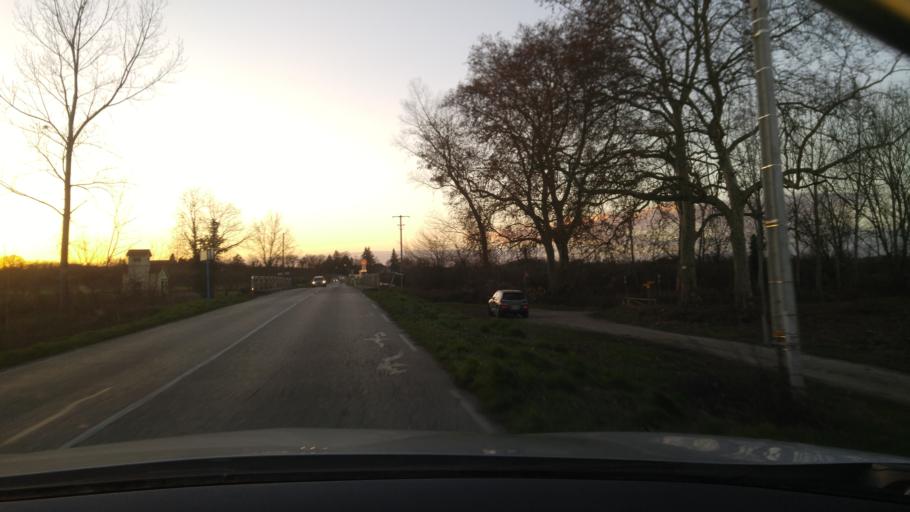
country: FR
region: Rhone-Alpes
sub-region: Departement de l'Isere
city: Tignieu-Jameyzieu
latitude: 45.7155
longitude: 5.1601
